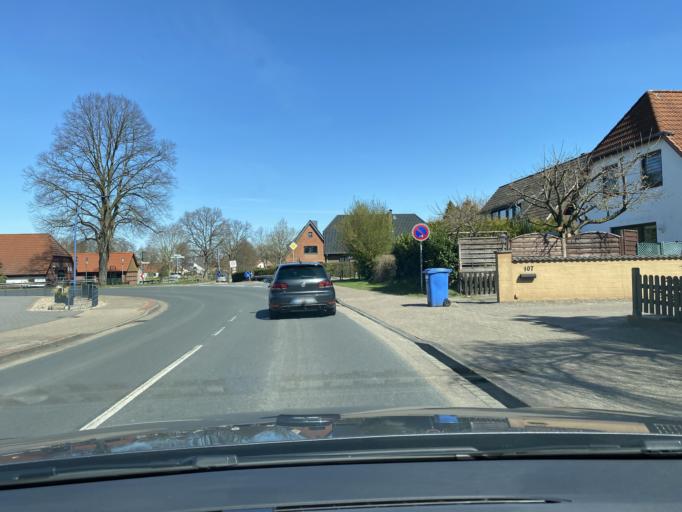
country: DE
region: Lower Saxony
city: Oyten
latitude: 53.0711
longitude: 9.0218
